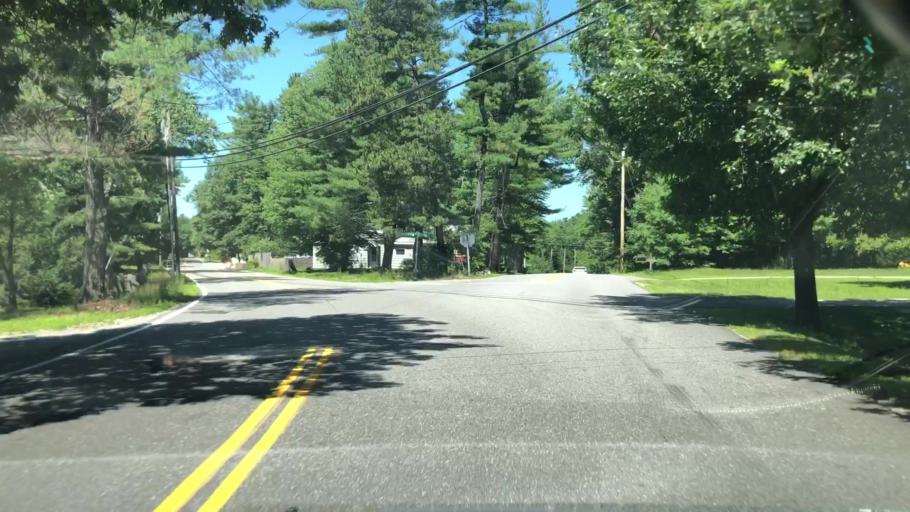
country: US
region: New Hampshire
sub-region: Hillsborough County
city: Milford
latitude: 42.8376
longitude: -71.5984
